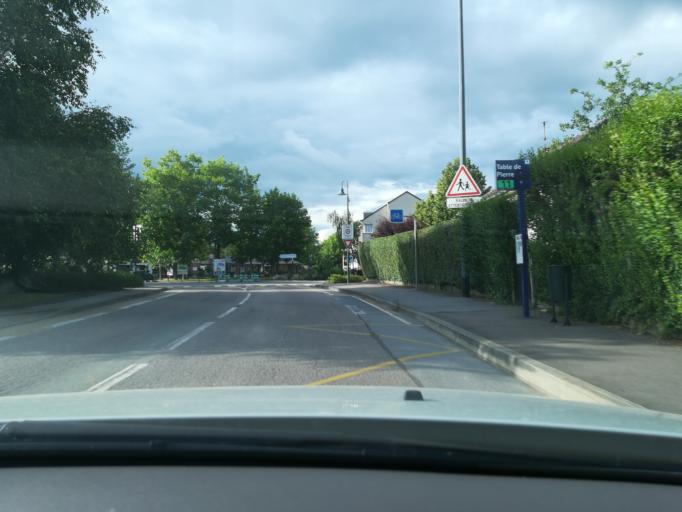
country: FR
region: Haute-Normandie
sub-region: Departement de la Seine-Maritime
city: Bois-Guillaume
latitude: 49.4784
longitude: 1.1131
